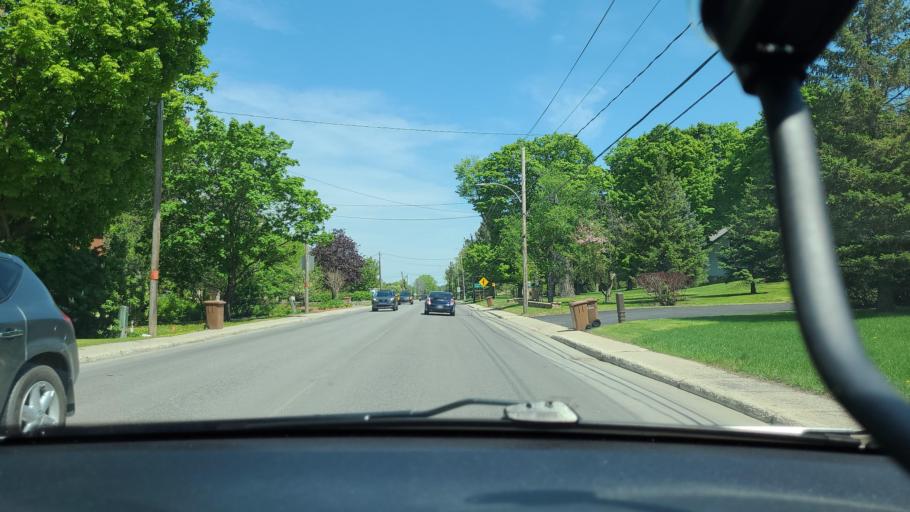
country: CA
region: Quebec
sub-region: Laurentides
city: Lachute
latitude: 45.6591
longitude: -74.3224
